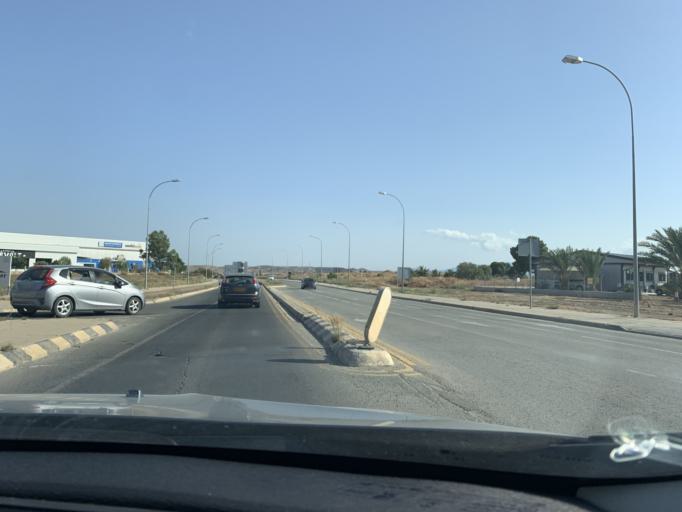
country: CY
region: Lefkosia
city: Nicosia
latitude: 35.1242
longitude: 33.3563
